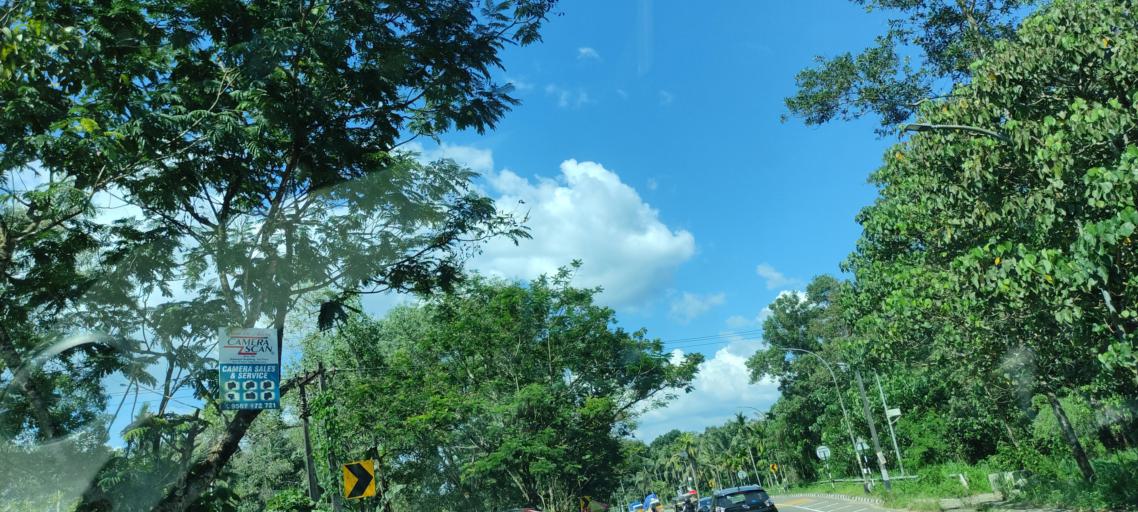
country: IN
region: Kerala
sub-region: Pattanamtitta
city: Adur
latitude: 9.1527
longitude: 76.7274
